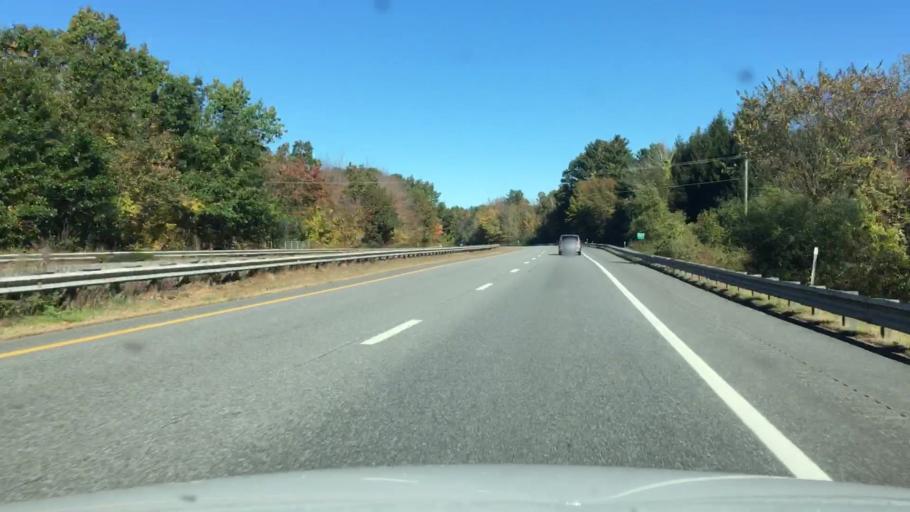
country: US
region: Maine
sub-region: York County
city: Eliot
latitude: 43.1470
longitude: -70.8431
